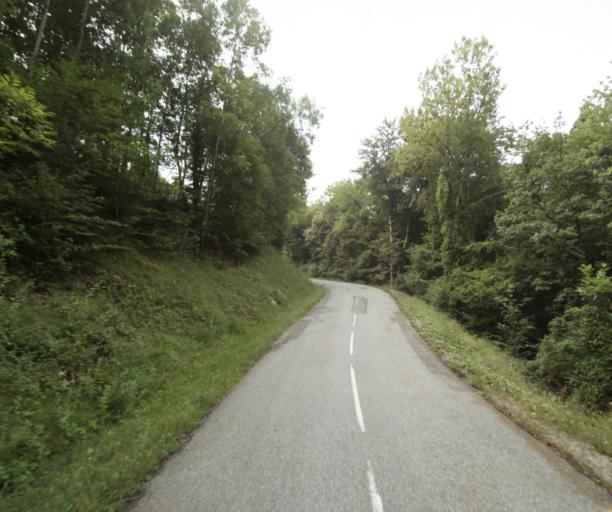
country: FR
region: Rhone-Alpes
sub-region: Departement de l'Isere
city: Saint-Egreve
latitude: 45.2700
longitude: 5.7081
